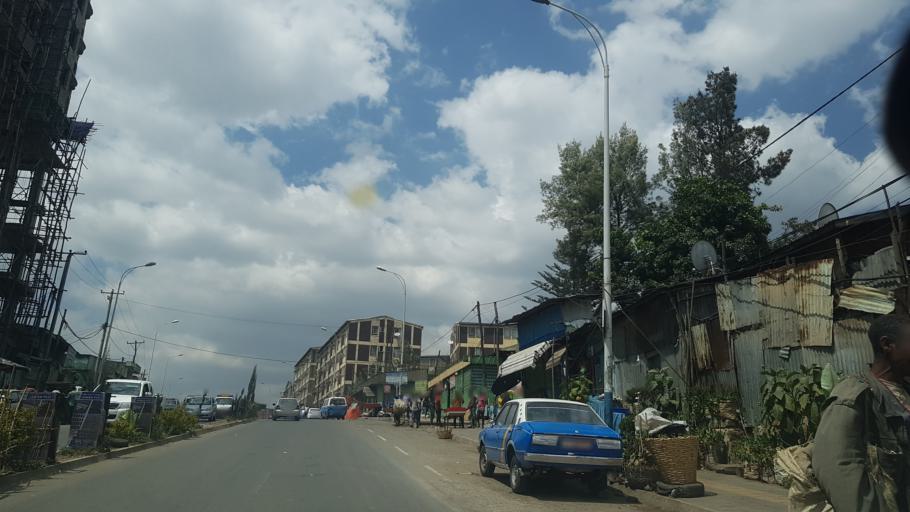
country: ET
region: Adis Abeba
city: Addis Ababa
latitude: 9.0283
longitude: 38.7470
